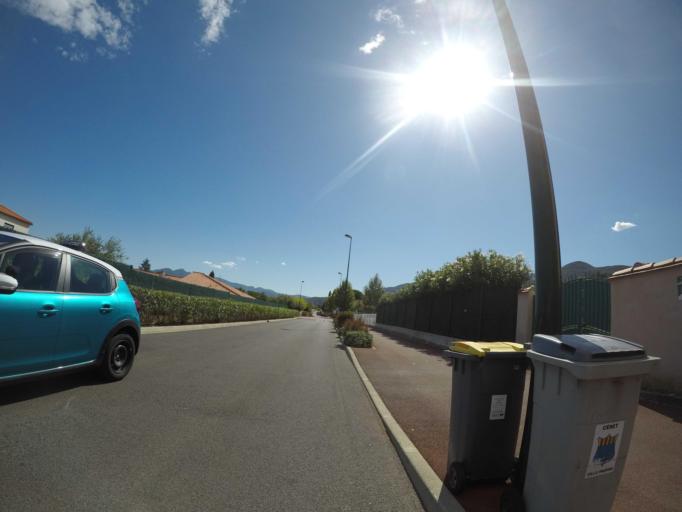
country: FR
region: Languedoc-Roussillon
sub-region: Departement des Pyrenees-Orientales
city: Ceret
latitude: 42.4925
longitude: 2.7371
